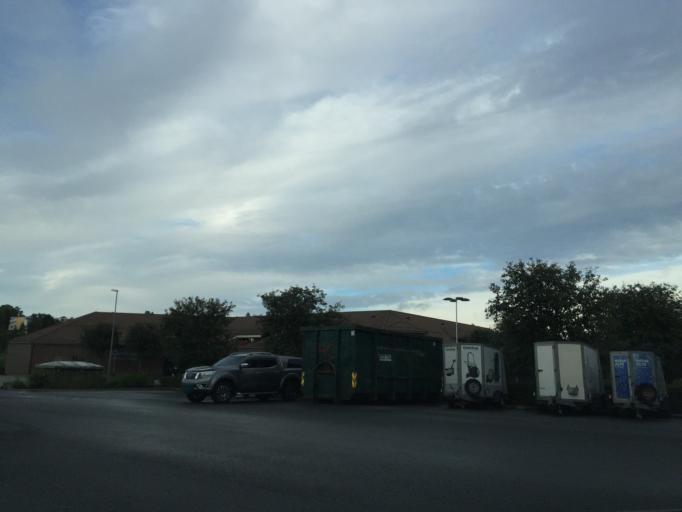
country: NO
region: Akershus
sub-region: Oppegard
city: Kolbotn
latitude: 59.8408
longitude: 10.8204
